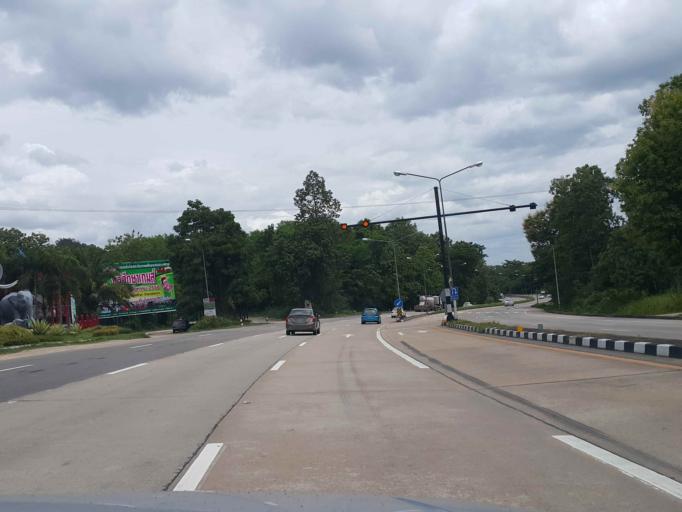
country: TH
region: Lampang
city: Hang Chat
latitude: 18.3547
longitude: 99.2430
